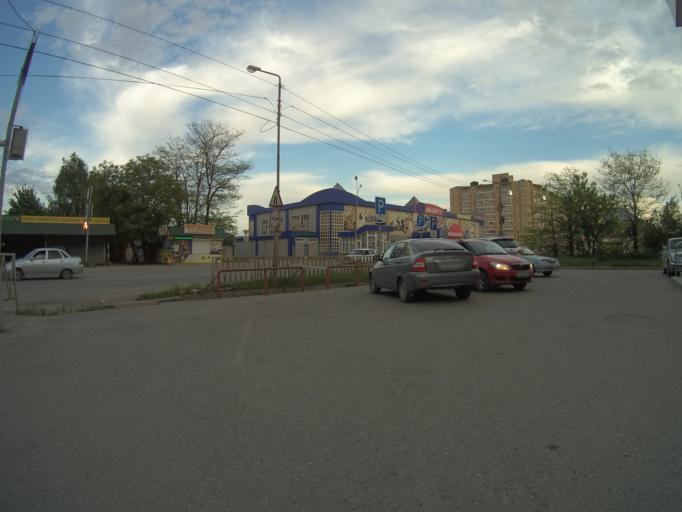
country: RU
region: Stavropol'skiy
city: Yessentukskaya
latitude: 44.0469
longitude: 42.8968
